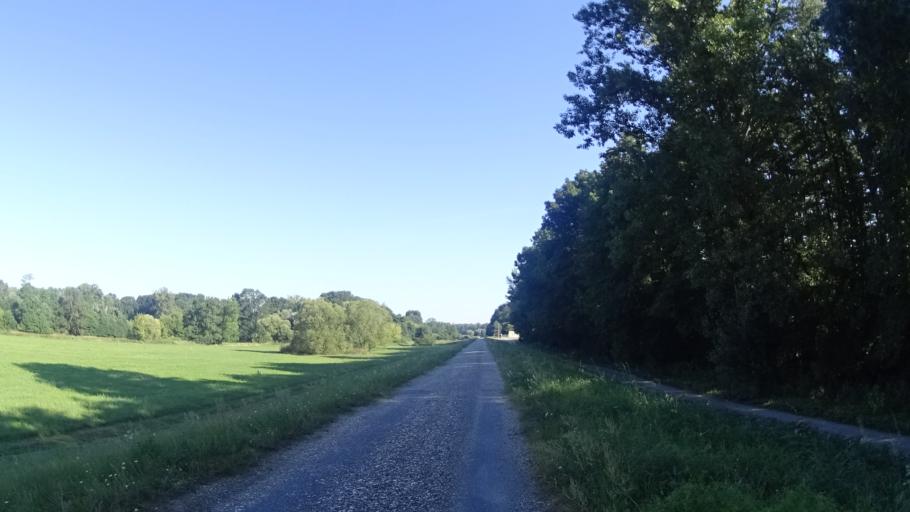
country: AT
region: Lower Austria
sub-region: Politischer Bezirk Mistelbach
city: Rabensburg
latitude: 48.6447
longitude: 16.9782
